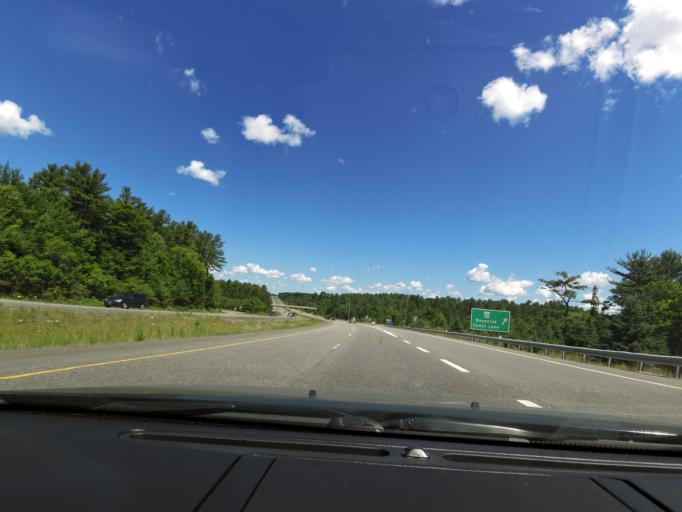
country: CA
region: Ontario
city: Bracebridge
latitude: 45.0825
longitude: -79.2965
